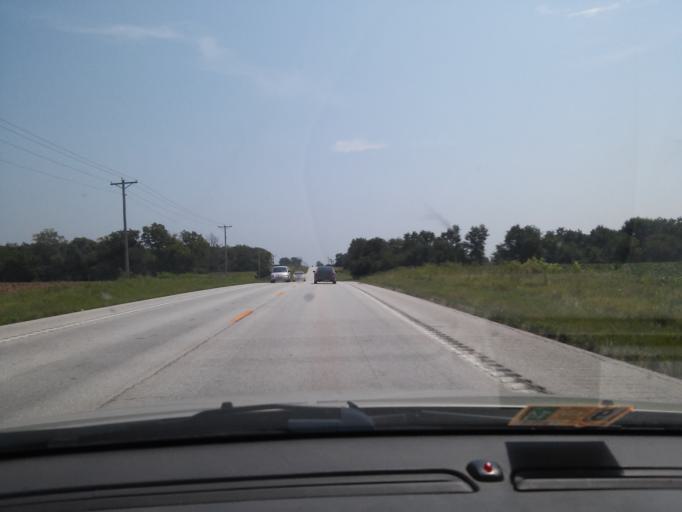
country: US
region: Missouri
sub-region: Pike County
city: Bowling Green
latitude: 39.3444
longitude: -91.2772
